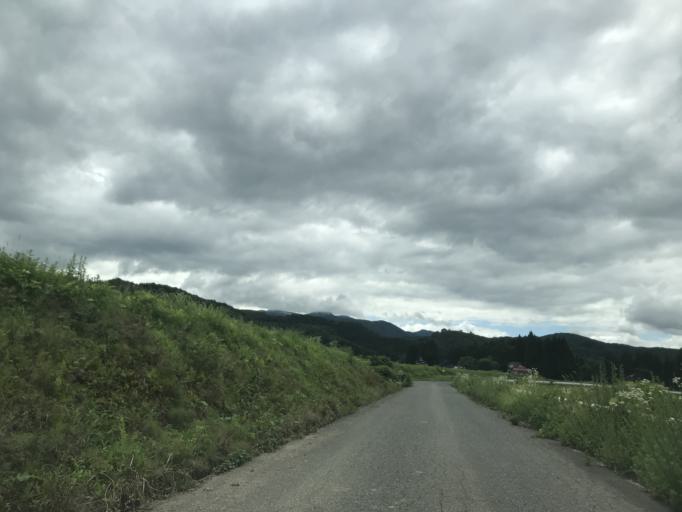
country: JP
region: Iwate
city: Ichinoseki
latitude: 38.9736
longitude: 140.9255
